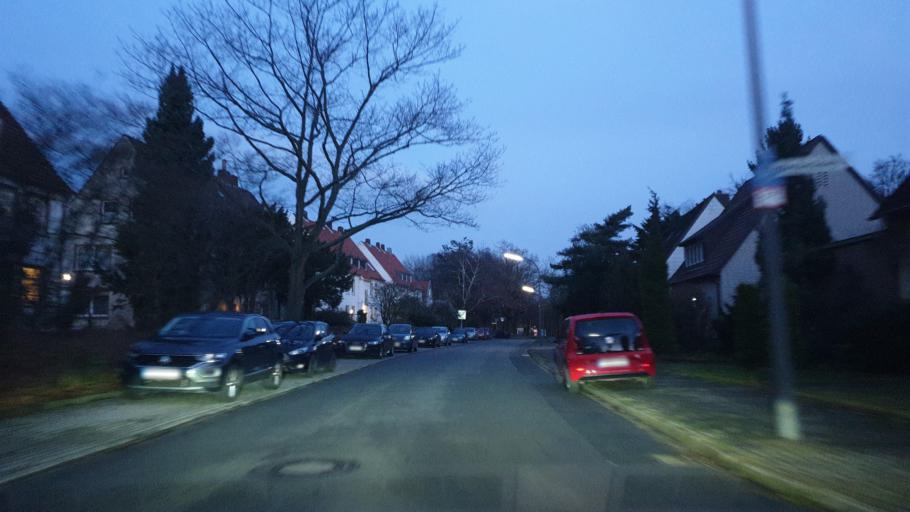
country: DE
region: Lower Saxony
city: Osnabrueck
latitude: 52.2696
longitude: 8.0146
